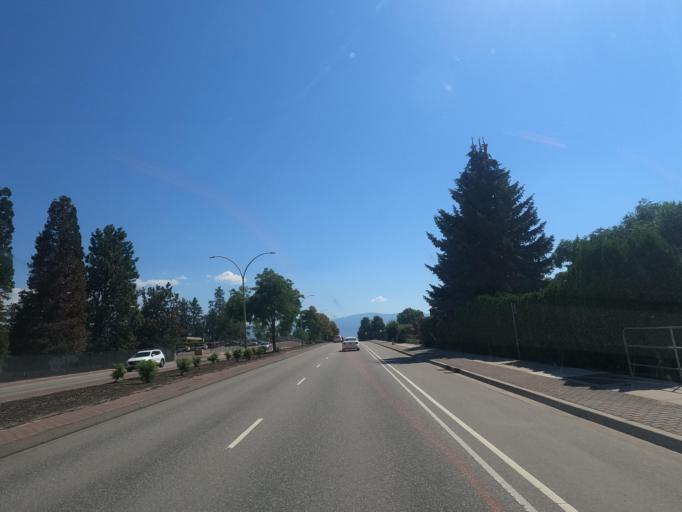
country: CA
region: British Columbia
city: Kelowna
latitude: 49.8930
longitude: -119.4546
